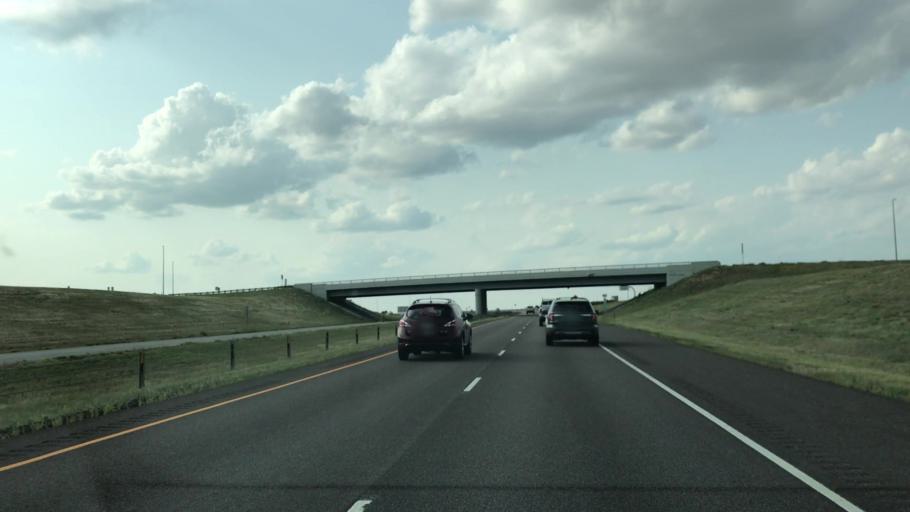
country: US
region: Colorado
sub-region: Adams County
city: Aurora
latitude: 39.8113
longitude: -104.7198
